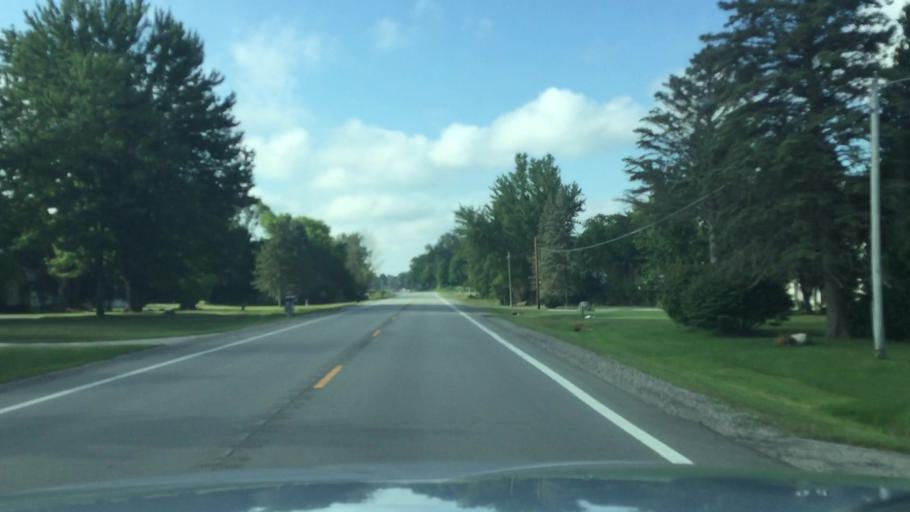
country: US
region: Michigan
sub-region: Genesee County
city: Clio
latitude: 43.2243
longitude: -83.7352
